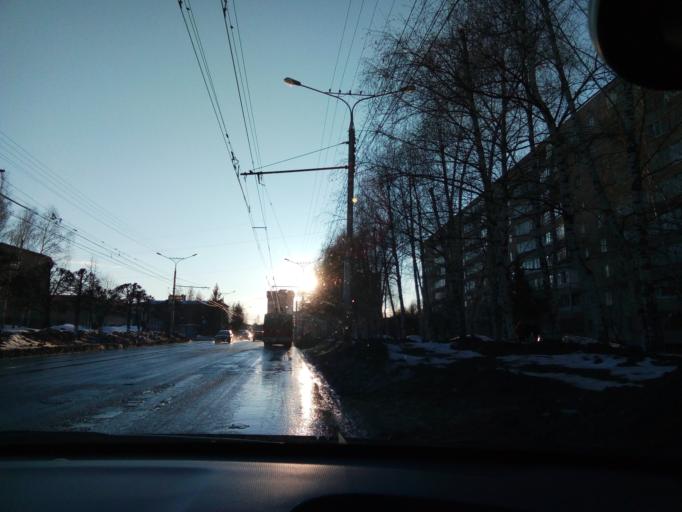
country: RU
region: Chuvashia
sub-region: Cheboksarskiy Rayon
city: Cheboksary
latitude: 56.1407
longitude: 47.1808
